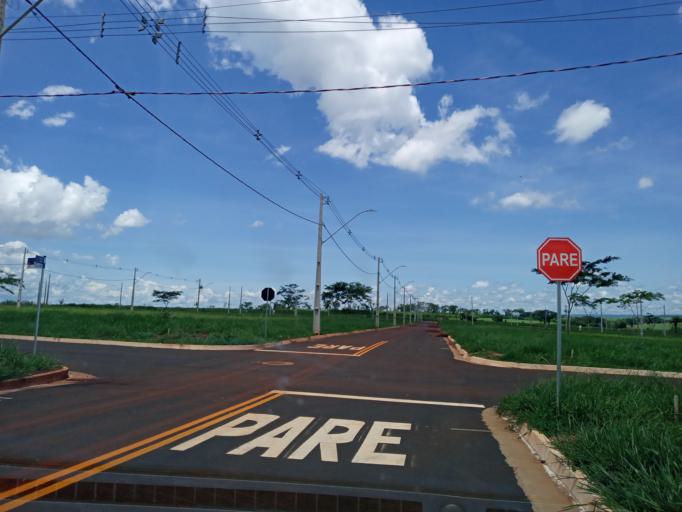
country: BR
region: Goias
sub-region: Itumbiara
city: Itumbiara
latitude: -18.4300
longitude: -49.1830
